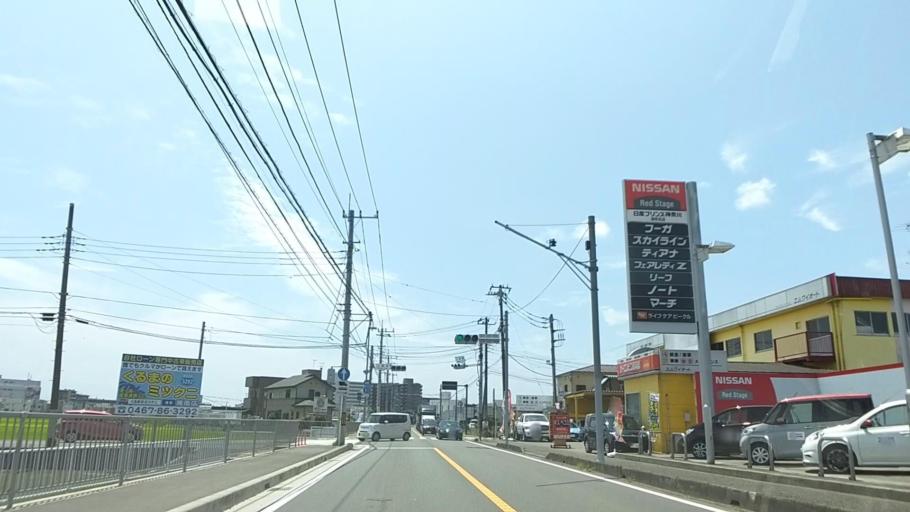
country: JP
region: Kanagawa
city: Atsugi
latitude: 35.4542
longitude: 139.3826
